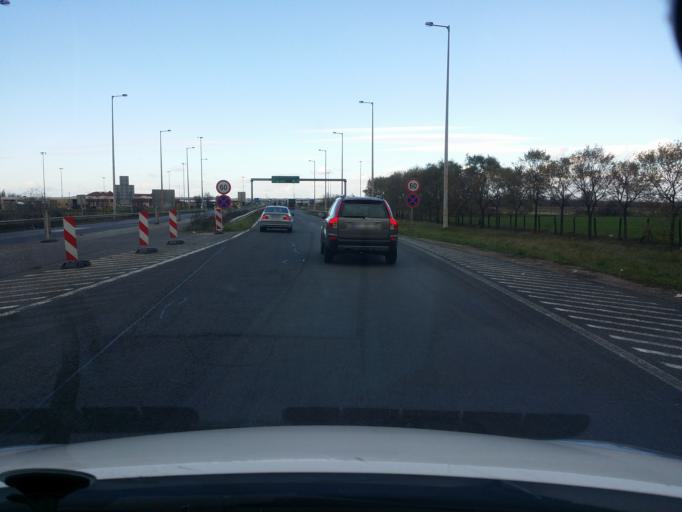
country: HU
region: Gyor-Moson-Sopron
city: Rajka
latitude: 48.0055
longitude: 17.1807
